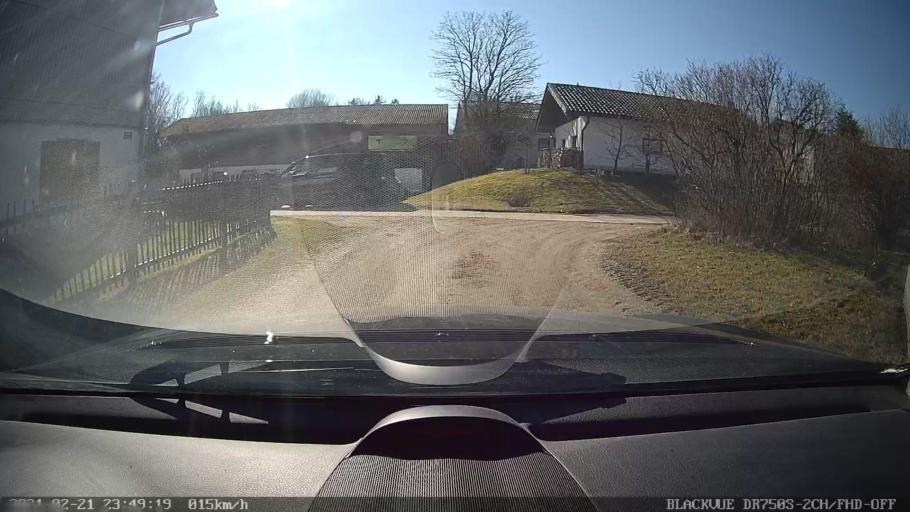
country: DE
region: Bavaria
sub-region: Upper Bavaria
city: Griesstatt
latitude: 47.9910
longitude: 12.2059
